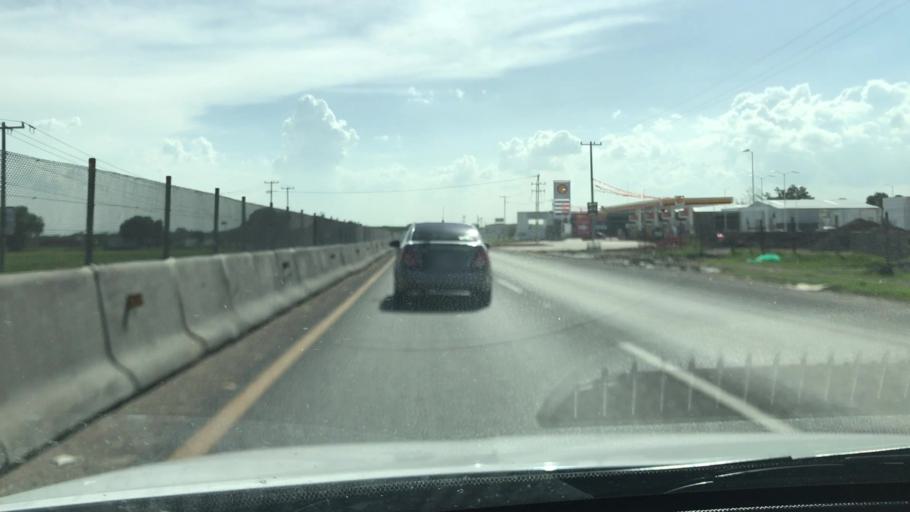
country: MX
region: Guanajuato
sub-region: Celaya
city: Colonia Pedro Maria Anaya
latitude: 20.5175
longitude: -100.8649
